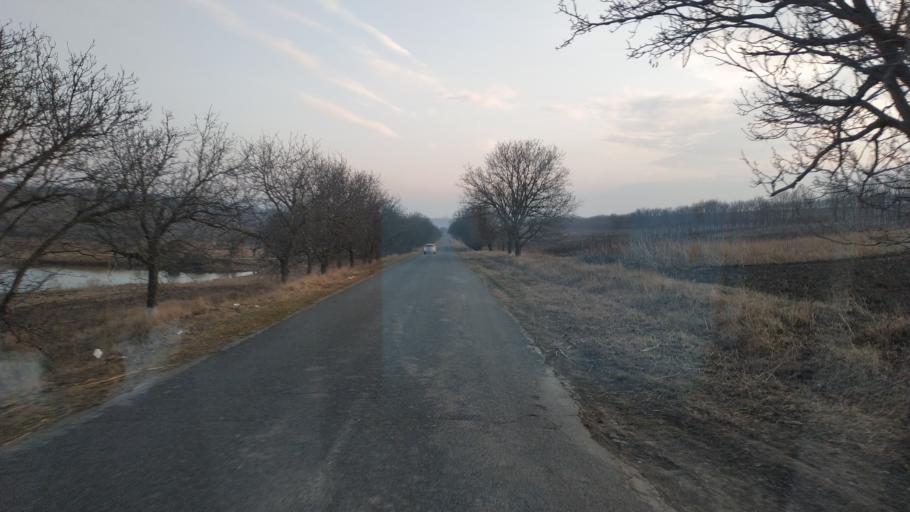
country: MD
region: Hincesti
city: Dancu
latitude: 46.6949
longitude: 28.3363
